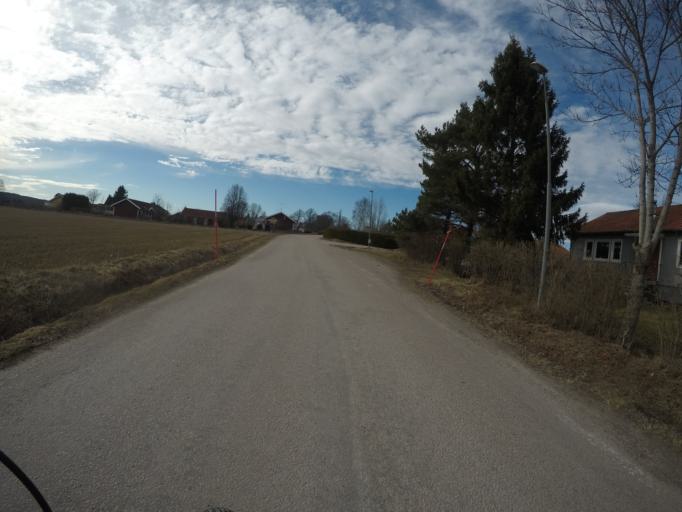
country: SE
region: Vaestmanland
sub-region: Kungsors Kommun
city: Kungsoer
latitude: 59.4182
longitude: 16.1945
